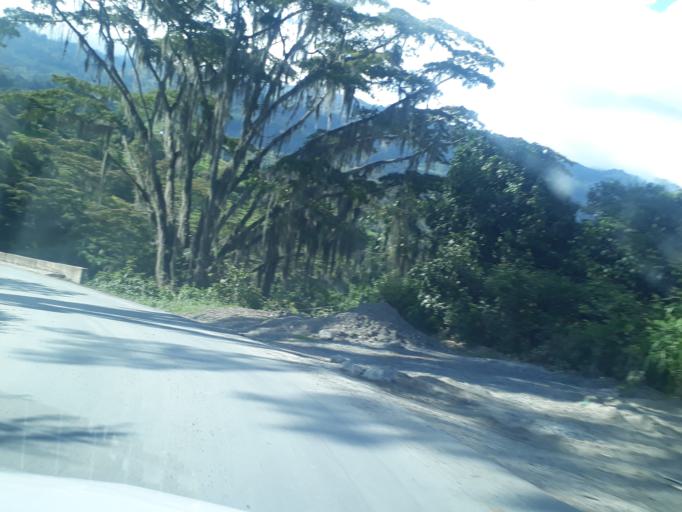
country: CO
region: Santander
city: Velez
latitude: 6.0400
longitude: -73.6523
